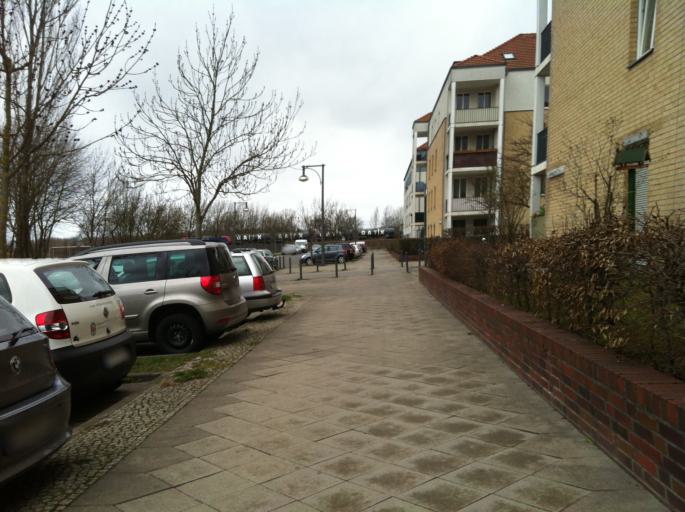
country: DE
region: Berlin
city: Karow
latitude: 52.6230
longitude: 13.4821
